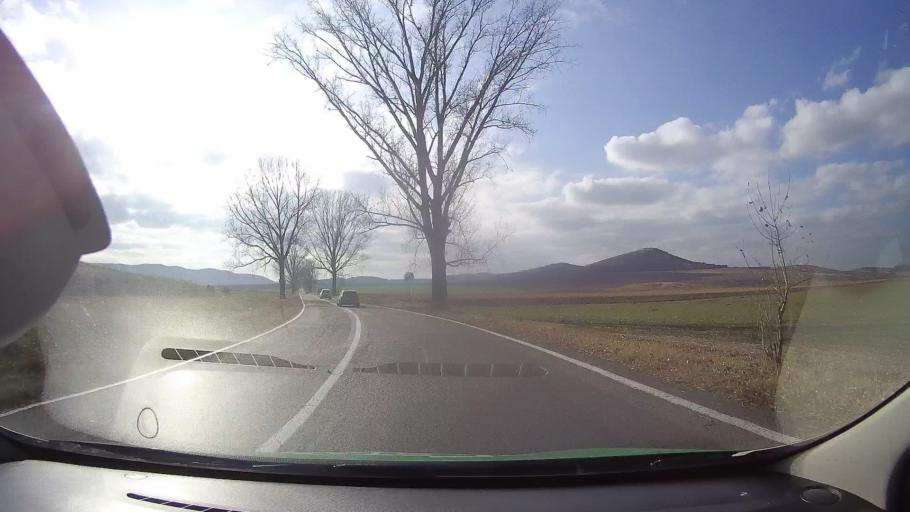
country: RO
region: Tulcea
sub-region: Comuna Nalbant
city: Nicolae Balcescu
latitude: 44.9927
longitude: 28.5650
